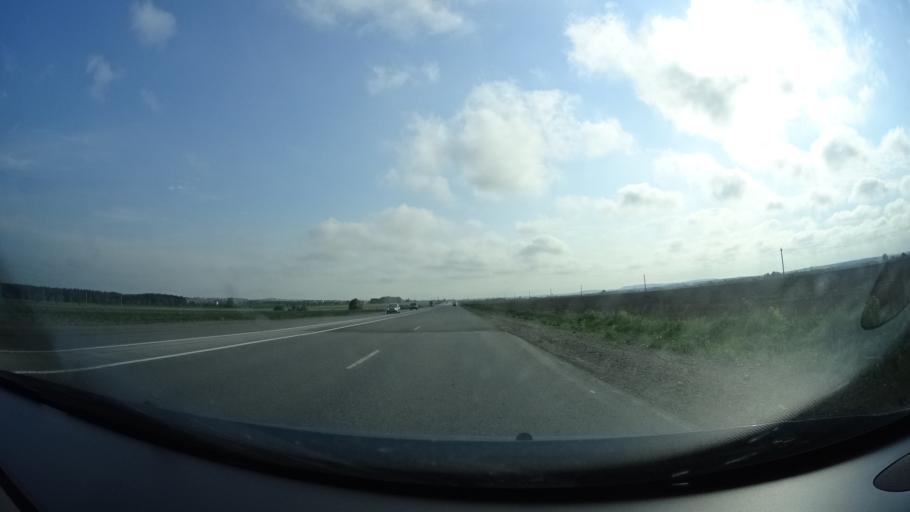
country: RU
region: Perm
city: Kultayevo
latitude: 57.8763
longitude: 55.9054
